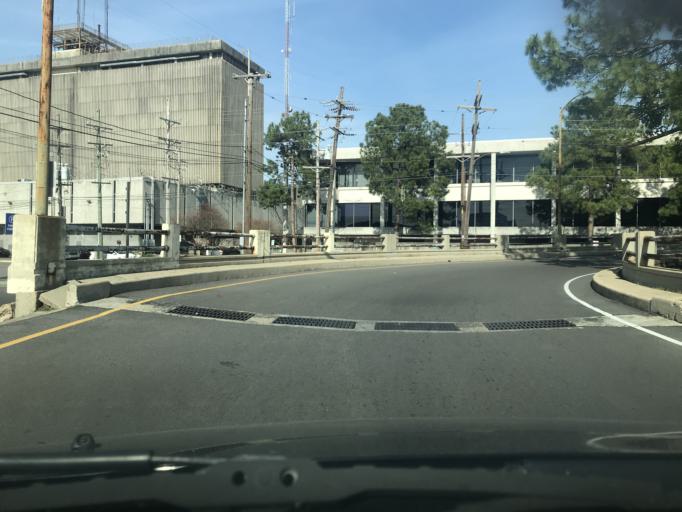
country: US
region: Louisiana
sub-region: Orleans Parish
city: New Orleans
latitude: 29.9595
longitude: -90.0934
